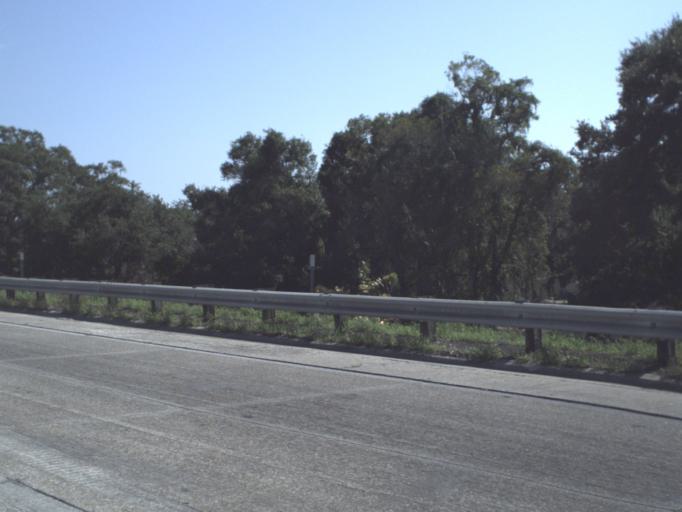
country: US
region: Florida
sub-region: Pinellas County
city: Saint Petersburg
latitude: 27.7506
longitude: -82.6770
